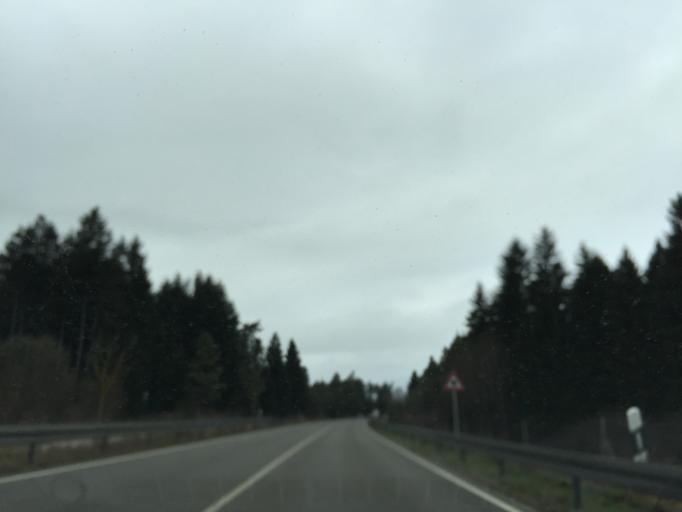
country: DE
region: Baden-Wuerttemberg
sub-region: Freiburg Region
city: Villingen-Schwenningen
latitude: 48.0362
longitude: 8.4987
